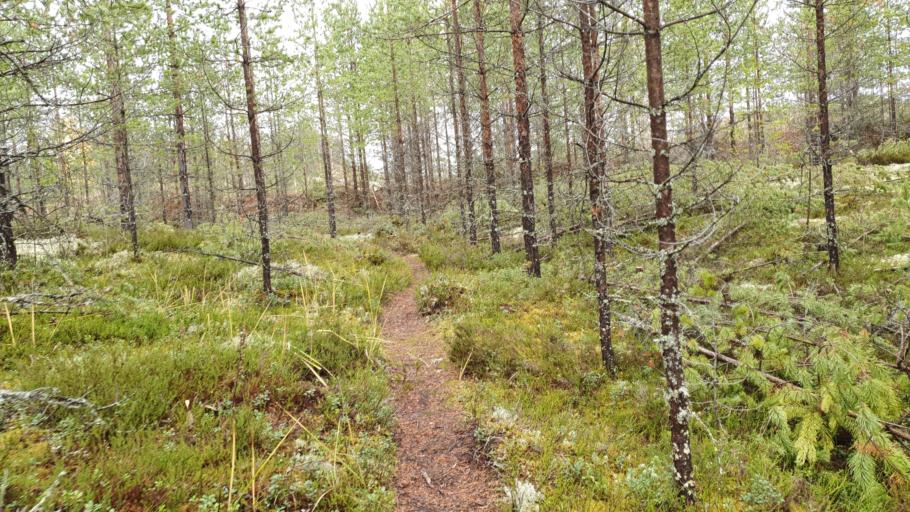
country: FI
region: Kainuu
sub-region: Kehys-Kainuu
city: Kuhmo
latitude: 64.1492
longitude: 29.4011
